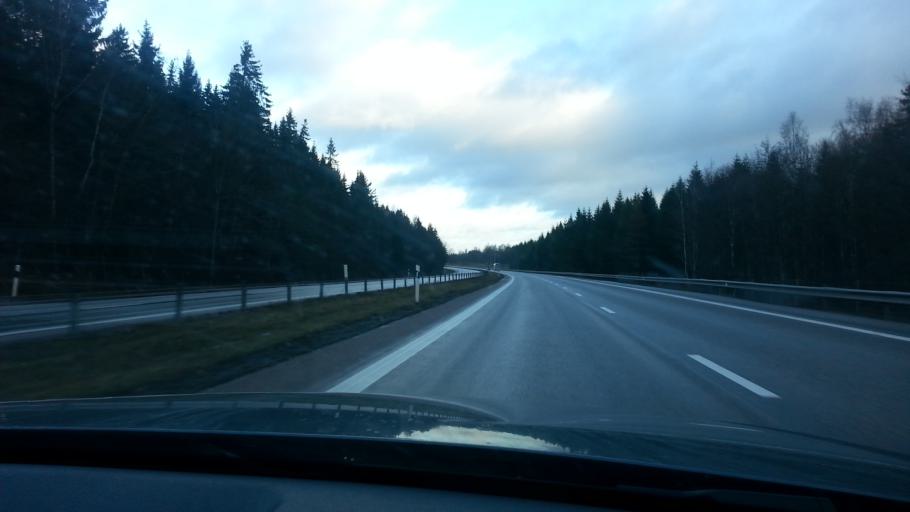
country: SE
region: OEstergoetland
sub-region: Odeshogs Kommun
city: OEdeshoeg
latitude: 58.1831
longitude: 14.6019
